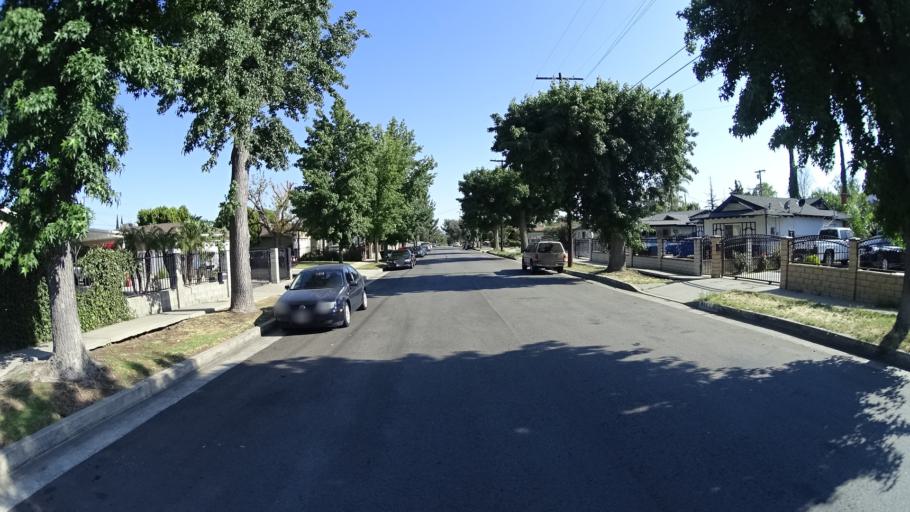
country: US
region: California
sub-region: Los Angeles County
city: Van Nuys
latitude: 34.2177
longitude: -118.4247
